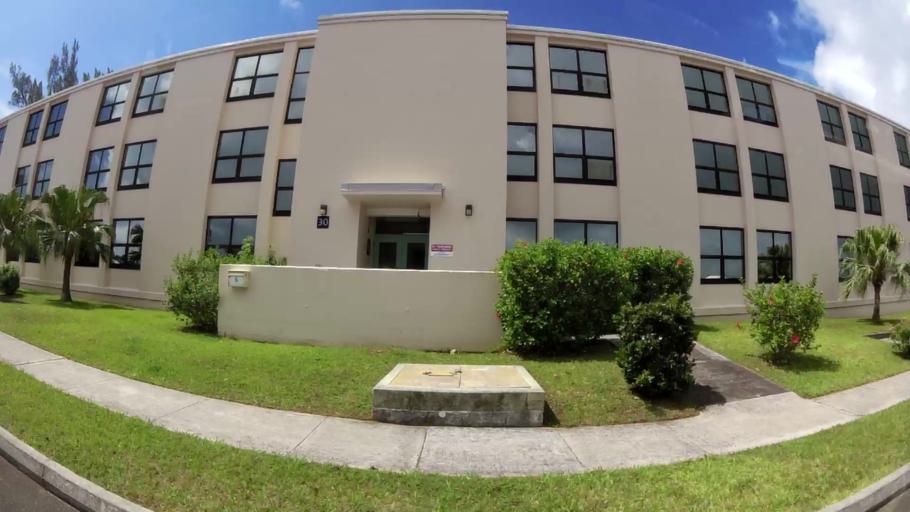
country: BM
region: Saint George
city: Saint George
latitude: 32.3636
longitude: -64.6607
